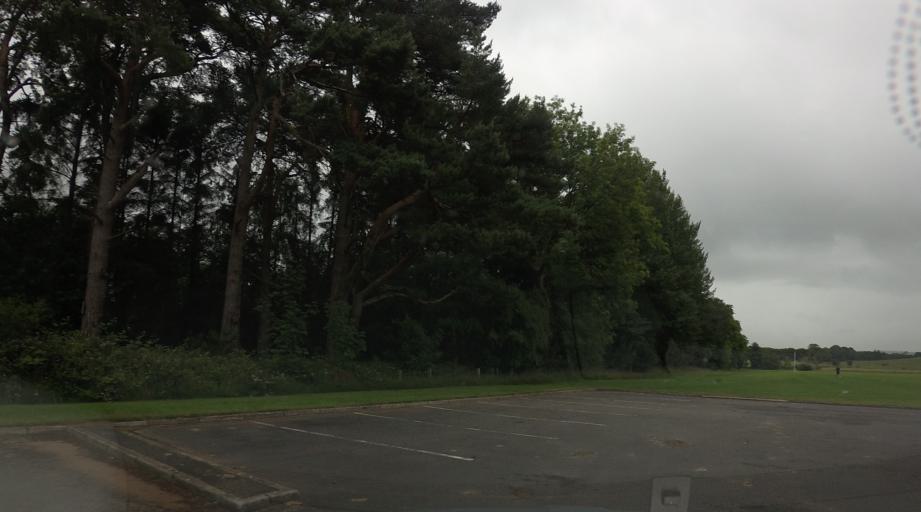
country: GB
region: Scotland
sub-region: South Ayrshire
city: Ayr
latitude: 55.4236
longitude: -4.6391
